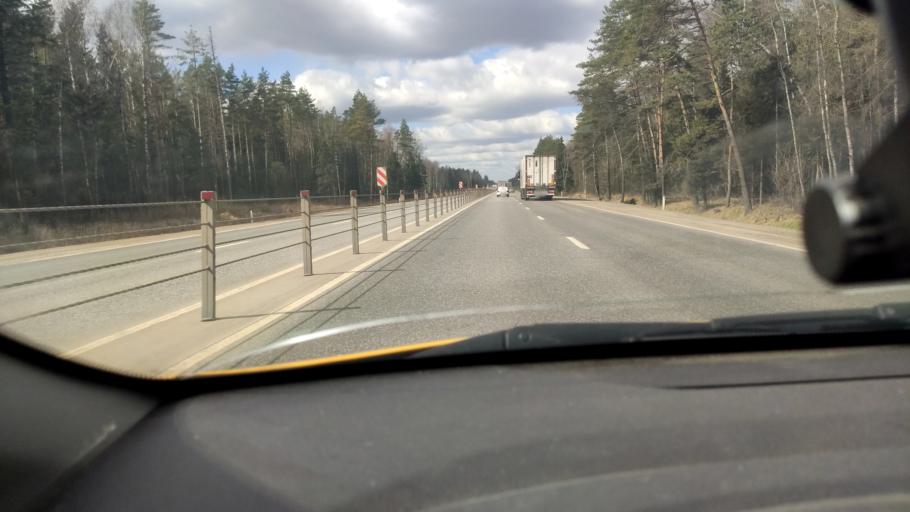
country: RU
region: Moskovskaya
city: Chupryakovo
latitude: 55.5640
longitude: 36.6233
